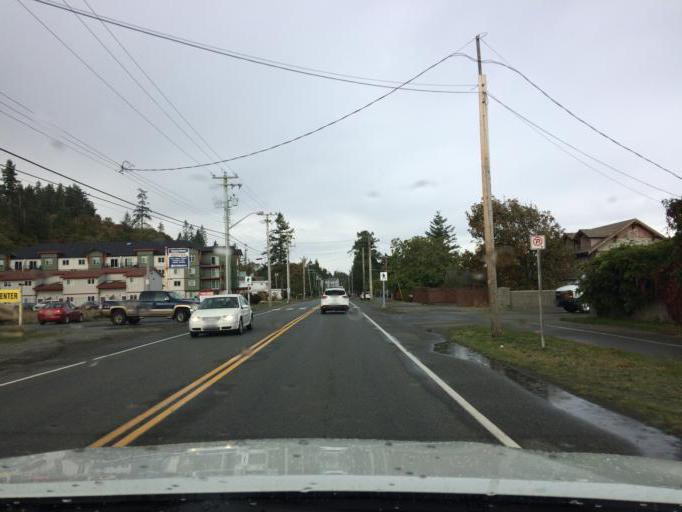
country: CA
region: British Columbia
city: Campbell River
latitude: 49.9916
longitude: -125.2277
